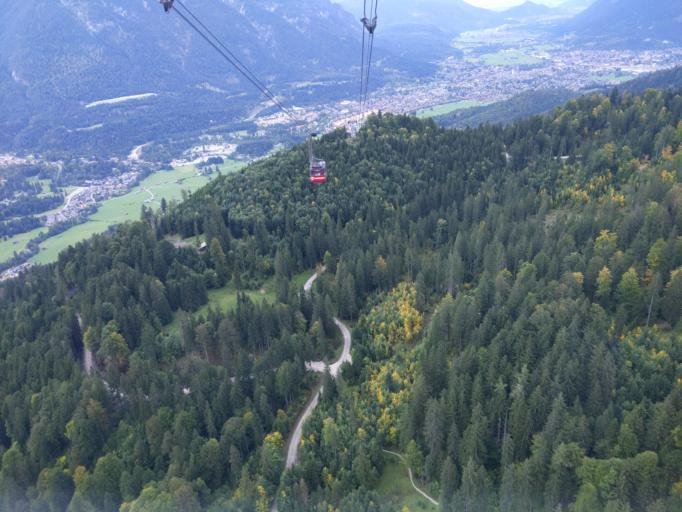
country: DE
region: Bavaria
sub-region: Upper Bavaria
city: Grainau
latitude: 47.4544
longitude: 11.0560
